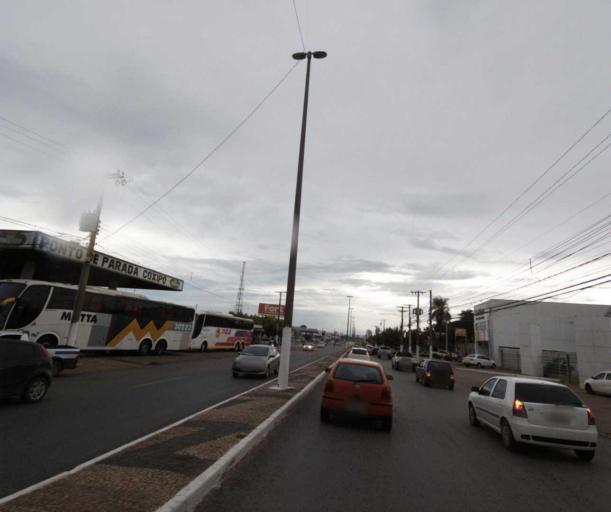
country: BR
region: Mato Grosso
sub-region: Cuiaba
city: Cuiaba
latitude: -15.6321
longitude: -56.0503
